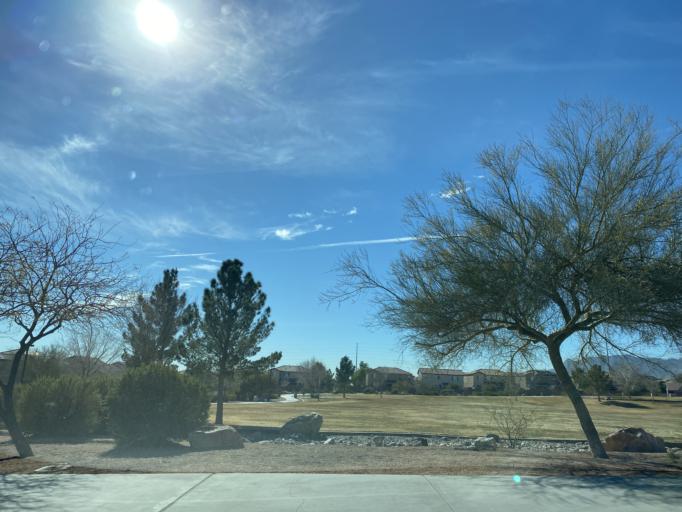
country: US
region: Nevada
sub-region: Clark County
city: Summerlin South
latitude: 36.3029
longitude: -115.3132
